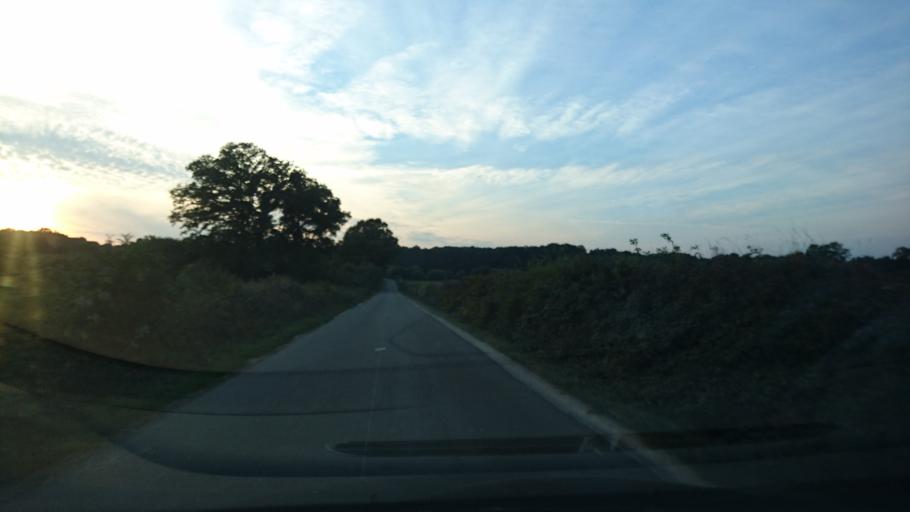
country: FR
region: Brittany
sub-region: Departement d'Ille-et-Vilaine
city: Maure-de-Bretagne
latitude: 47.8657
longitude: -2.0505
